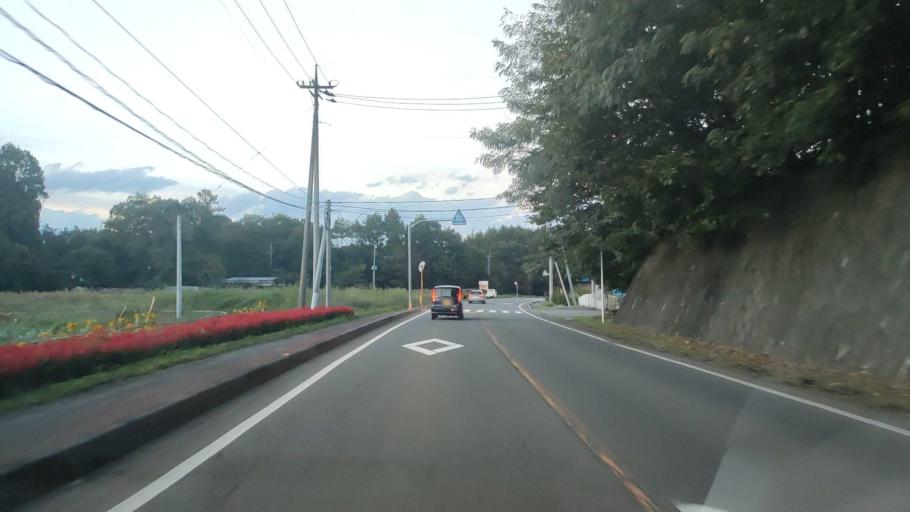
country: JP
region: Nagano
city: Komoro
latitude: 36.5103
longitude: 138.5943
